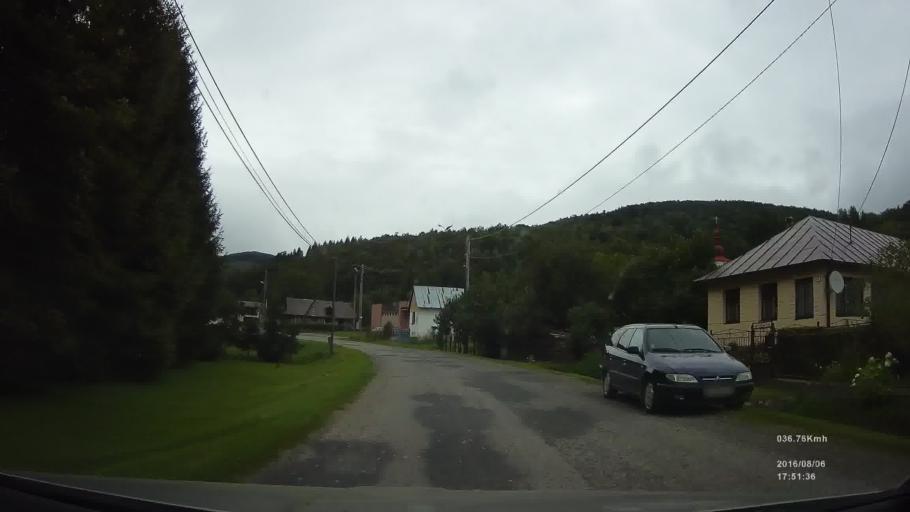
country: SK
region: Presovsky
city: Svidnik
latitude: 49.4014
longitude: 21.5702
